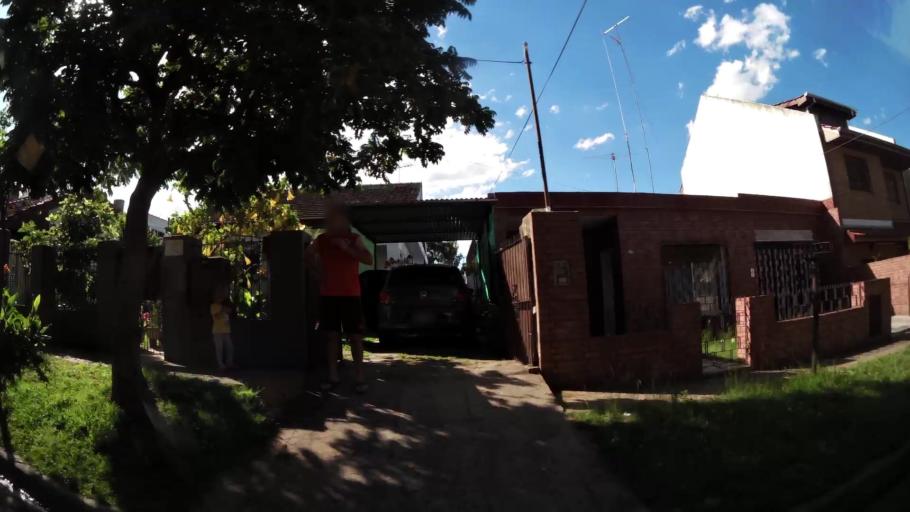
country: AR
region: Buenos Aires
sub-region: Partido de San Isidro
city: San Isidro
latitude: -34.4721
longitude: -58.5584
